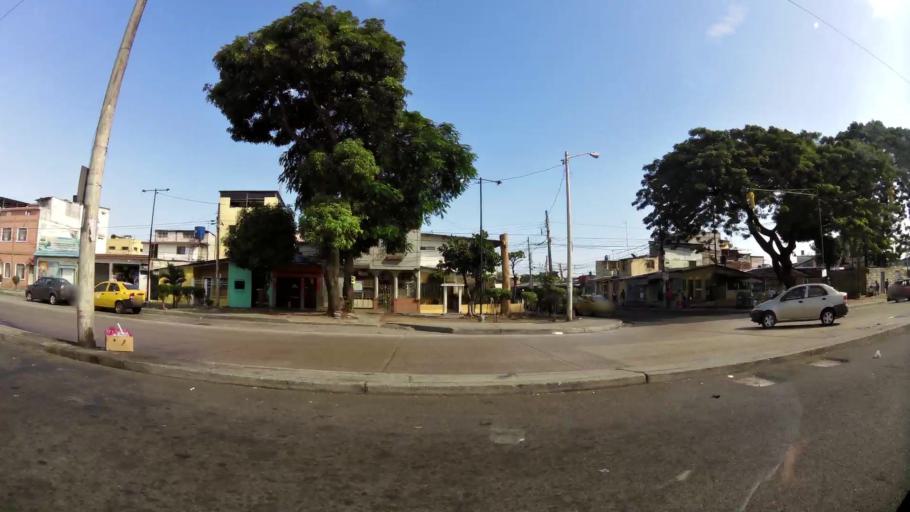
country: EC
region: Guayas
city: Guayaquil
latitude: -2.2212
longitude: -79.9044
